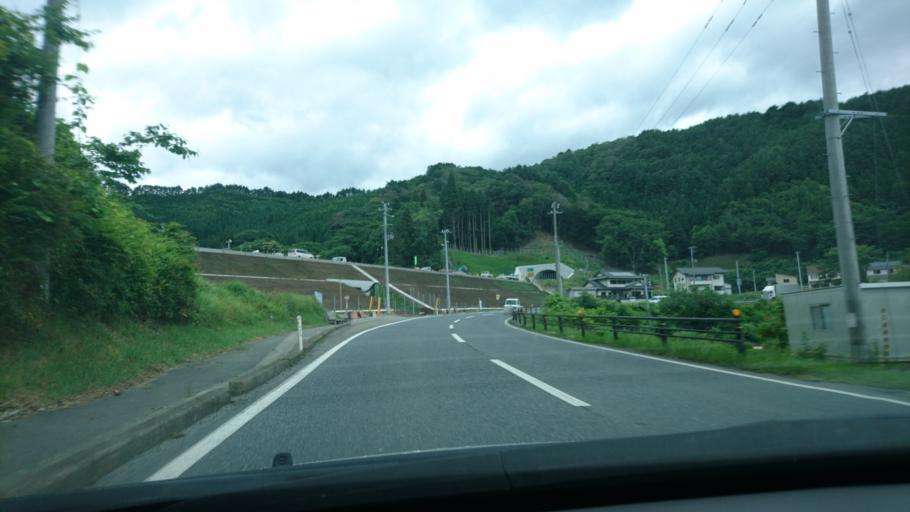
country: JP
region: Iwate
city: Kamaishi
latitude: 39.2101
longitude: 141.8645
